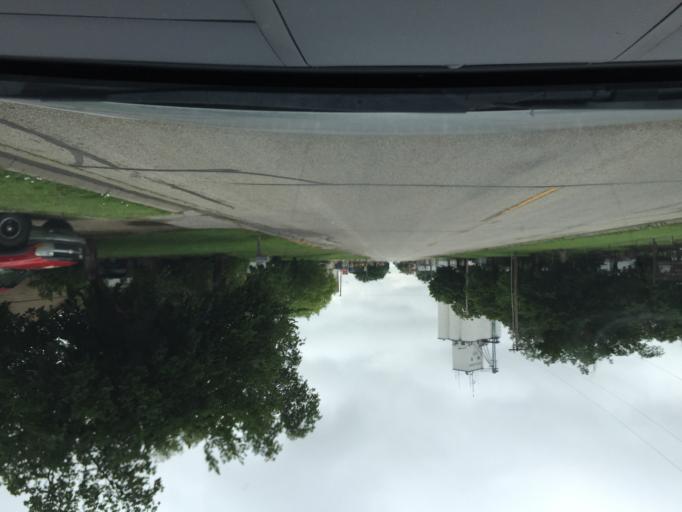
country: US
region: Kansas
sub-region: McPherson County
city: Moundridge
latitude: 38.2030
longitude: -97.5255
